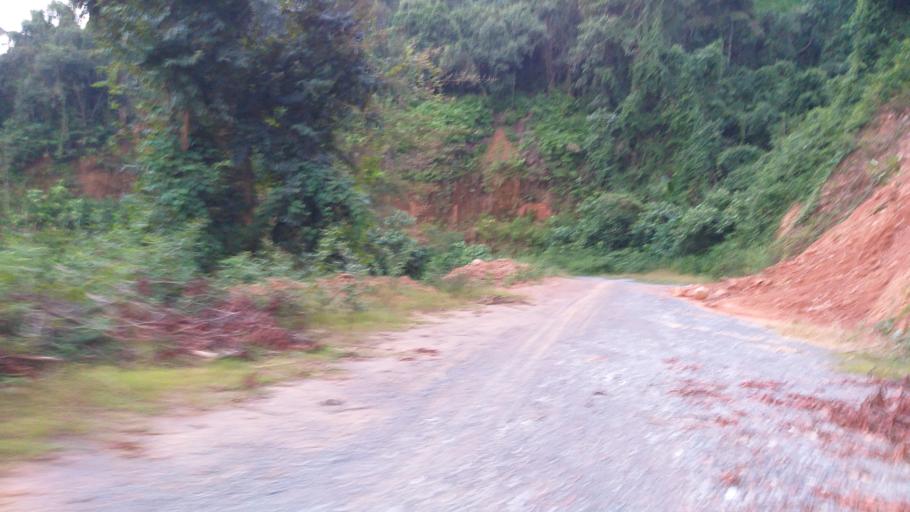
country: LA
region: Phongsali
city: Khoa
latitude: 21.1844
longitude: 102.5130
